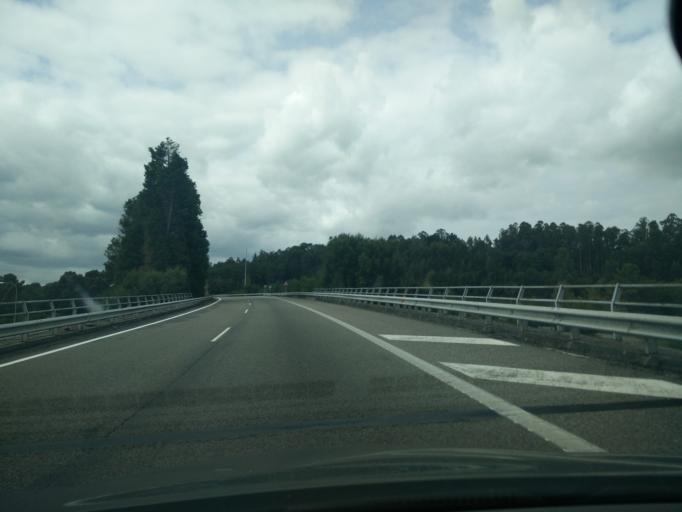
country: ES
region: Galicia
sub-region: Provincia da Coruna
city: Bergondo
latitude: 43.2886
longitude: -8.2815
